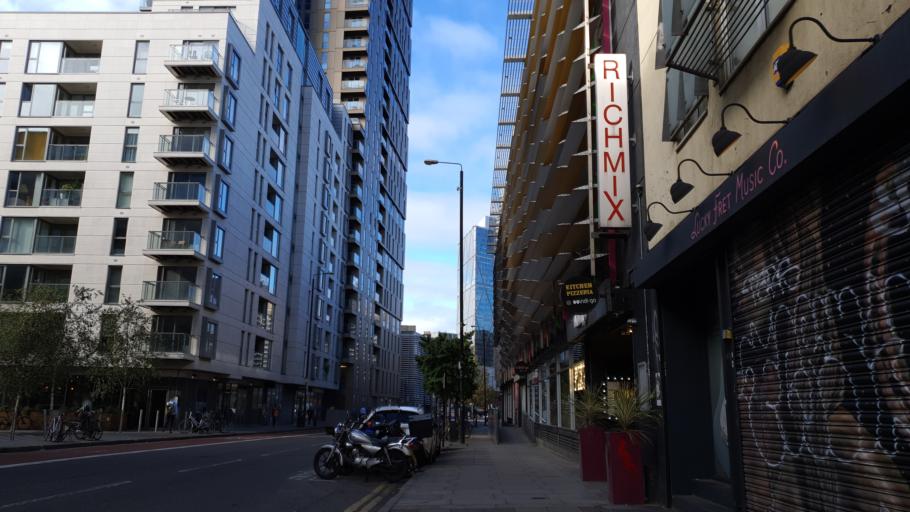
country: GB
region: England
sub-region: Greater London
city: Bethnal Green
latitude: 51.5245
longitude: -0.0726
